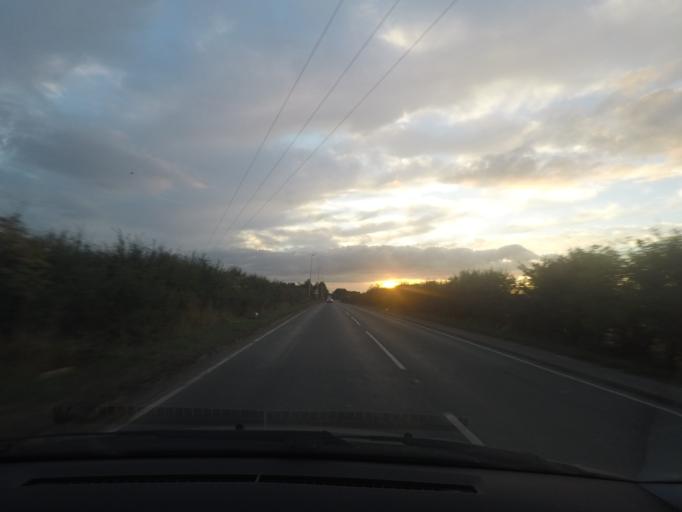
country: GB
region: England
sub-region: North Lincolnshire
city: Barnetby le Wold
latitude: 53.5824
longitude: -0.4044
